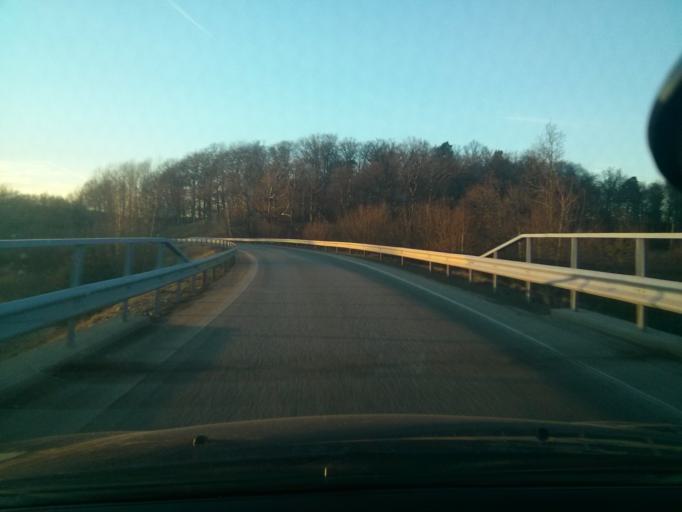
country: SE
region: Blekinge
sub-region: Karlskrona Kommun
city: Rodeby
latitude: 56.2133
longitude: 15.5930
